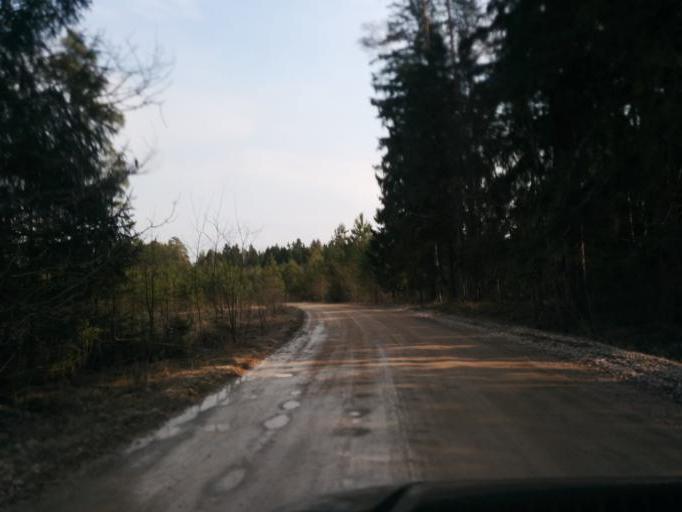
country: LV
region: Olaine
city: Olaine
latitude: 56.7893
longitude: 24.0431
